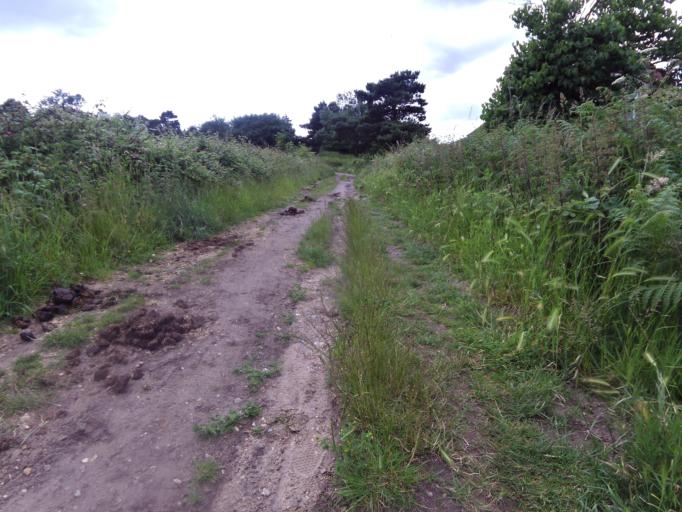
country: GB
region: England
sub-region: Norfolk
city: Sheringham
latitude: 52.9327
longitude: 1.1504
